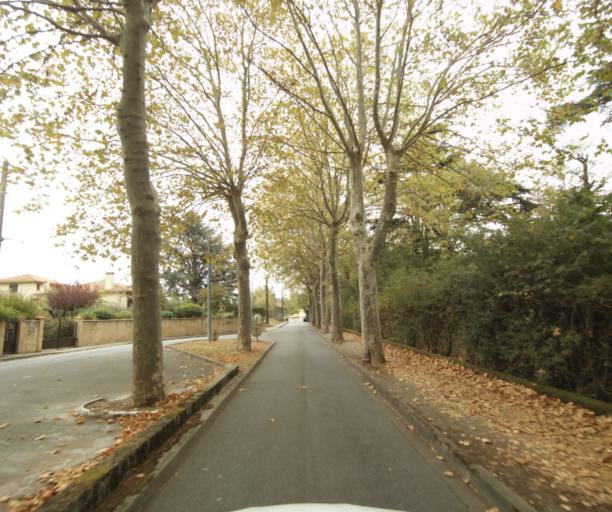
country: FR
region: Midi-Pyrenees
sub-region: Departement de la Haute-Garonne
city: Villefranche-de-Lauragais
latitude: 43.4056
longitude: 1.7148
